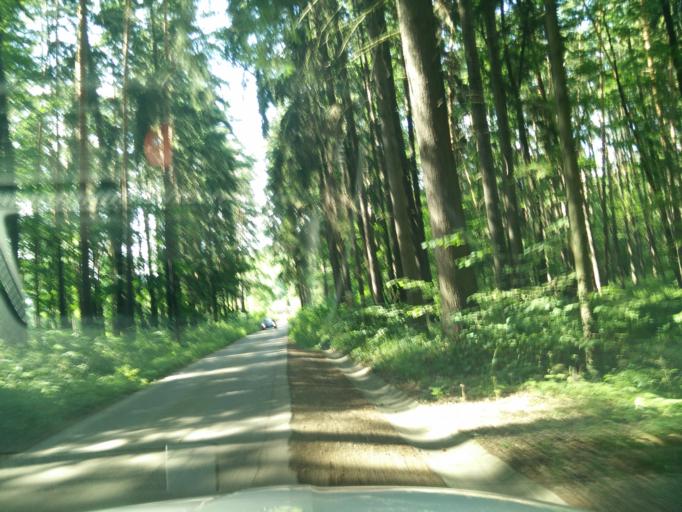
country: SK
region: Nitriansky
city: Prievidza
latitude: 48.7458
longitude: 18.6358
